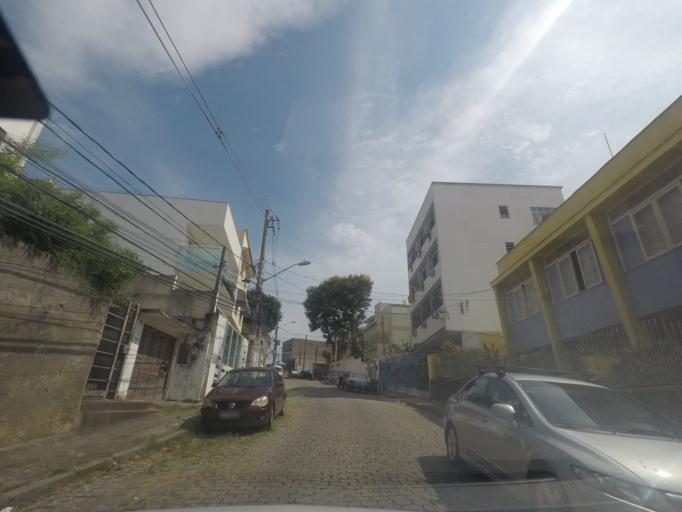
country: BR
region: Rio de Janeiro
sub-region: Rio De Janeiro
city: Rio de Janeiro
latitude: -22.8170
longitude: -43.1957
